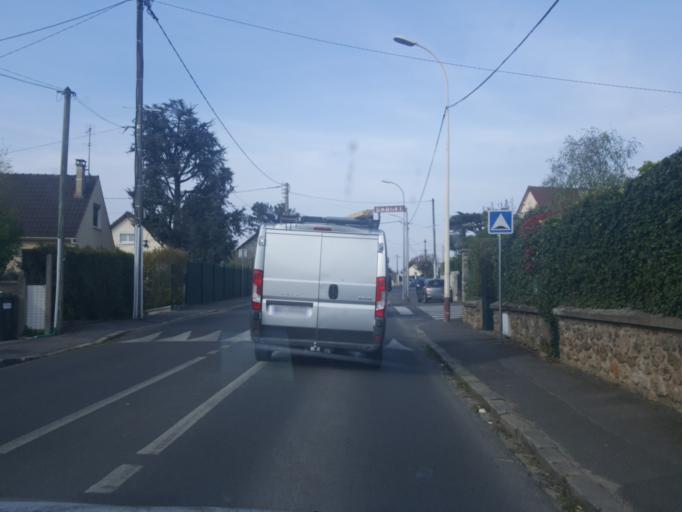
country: FR
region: Ile-de-France
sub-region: Departement de l'Essonne
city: Longpont-sur-Orge
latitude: 48.6469
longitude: 2.3019
